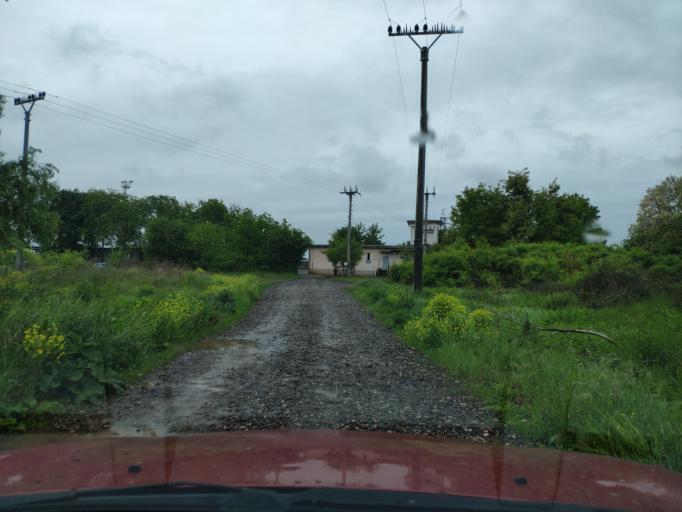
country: SK
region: Kosicky
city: Cierna nad Tisou
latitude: 48.4244
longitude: 22.0828
